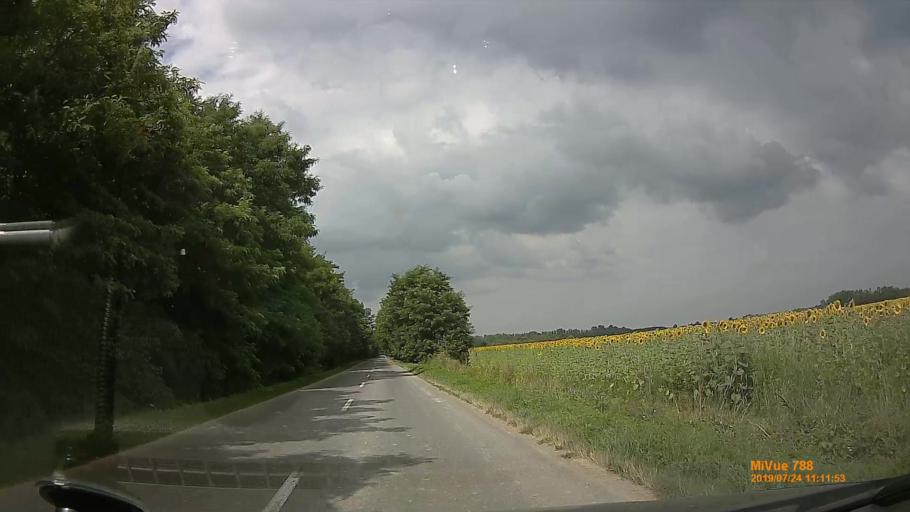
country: HU
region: Szabolcs-Szatmar-Bereg
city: Tarpa
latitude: 48.2032
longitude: 22.4647
